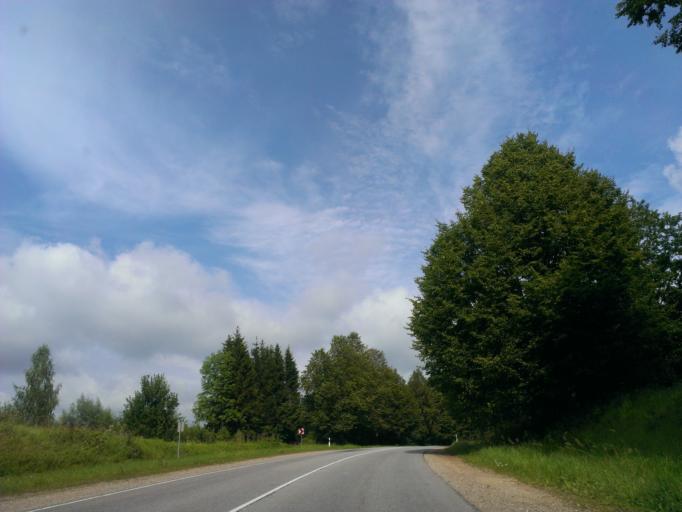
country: LV
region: Amatas Novads
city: Drabesi
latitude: 57.2363
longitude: 25.2754
